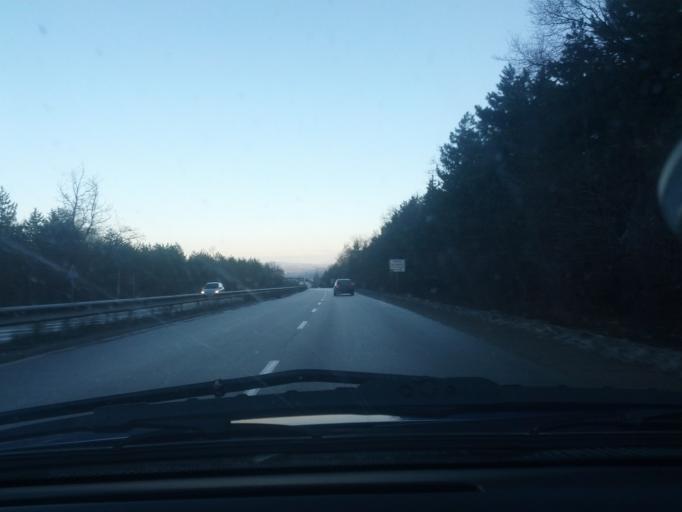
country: BG
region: Vratsa
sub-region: Obshtina Vratsa
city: Vratsa
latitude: 43.1814
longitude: 23.5933
